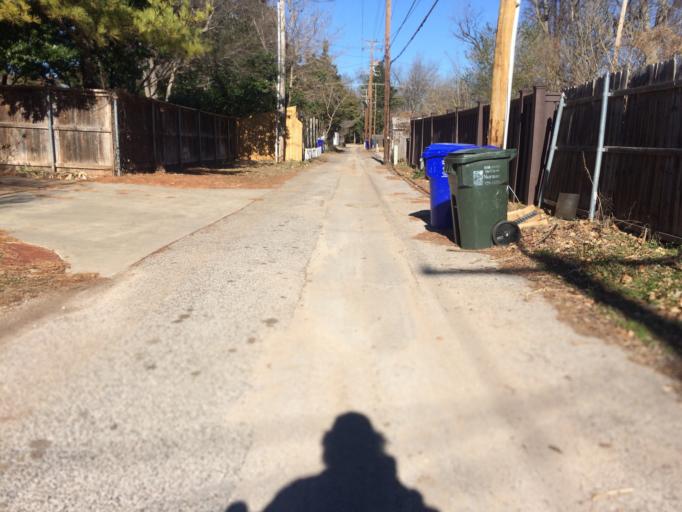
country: US
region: Oklahoma
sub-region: Cleveland County
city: Norman
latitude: 35.2063
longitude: -97.4523
